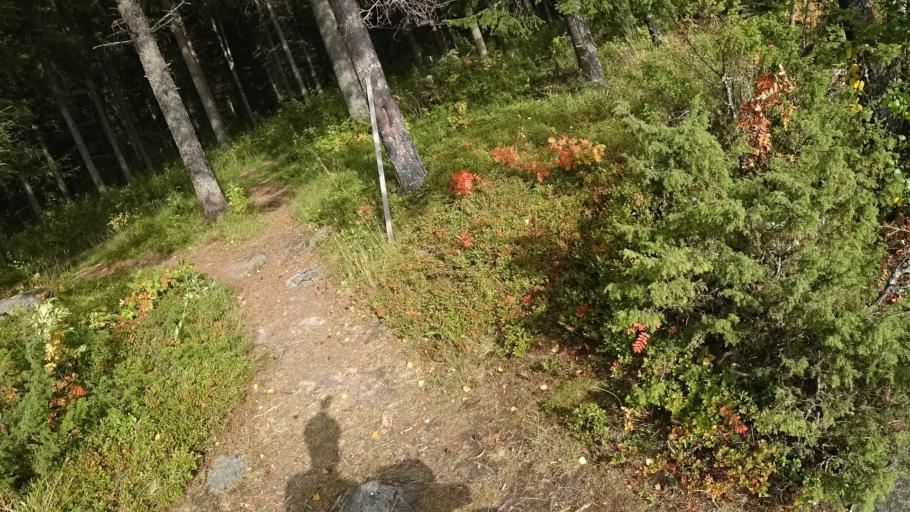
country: FI
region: North Karelia
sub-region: Joensuu
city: Ilomantsi
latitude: 62.6685
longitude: 30.9060
